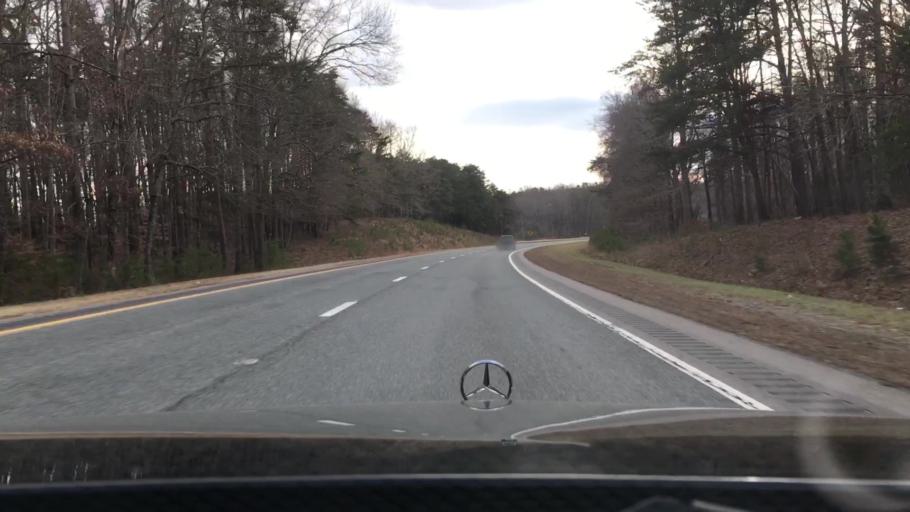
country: US
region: Virginia
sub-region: Pittsylvania County
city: Gretna
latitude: 36.9288
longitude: -79.3763
